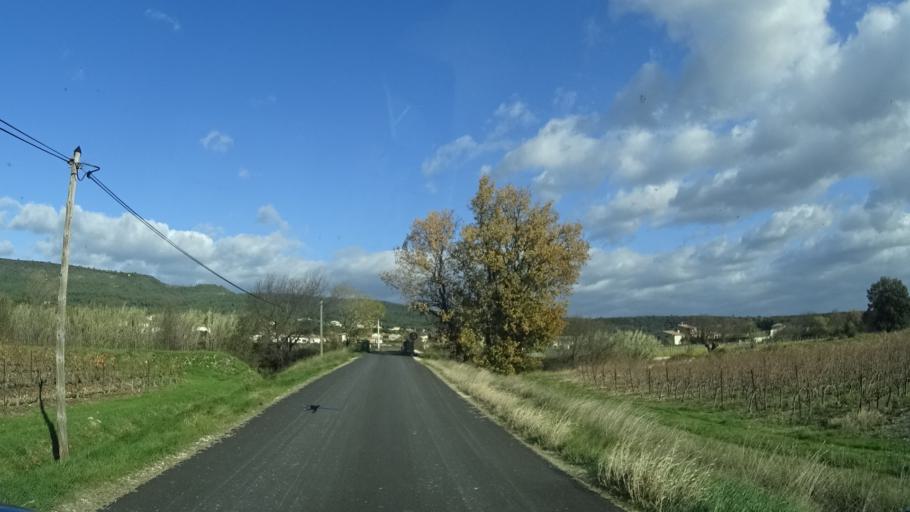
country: FR
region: Languedoc-Roussillon
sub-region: Departement de l'Herault
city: Claret
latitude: 43.8571
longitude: 3.8974
